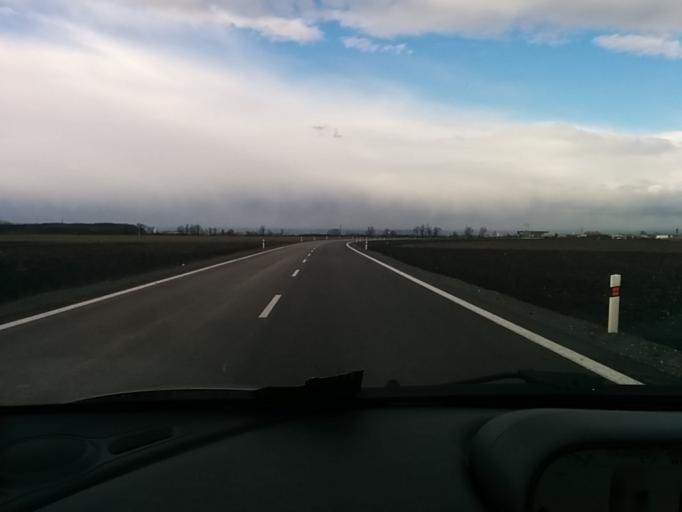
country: SK
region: Trnavsky
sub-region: Okres Galanta
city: Galanta
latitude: 48.2703
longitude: 17.7017
